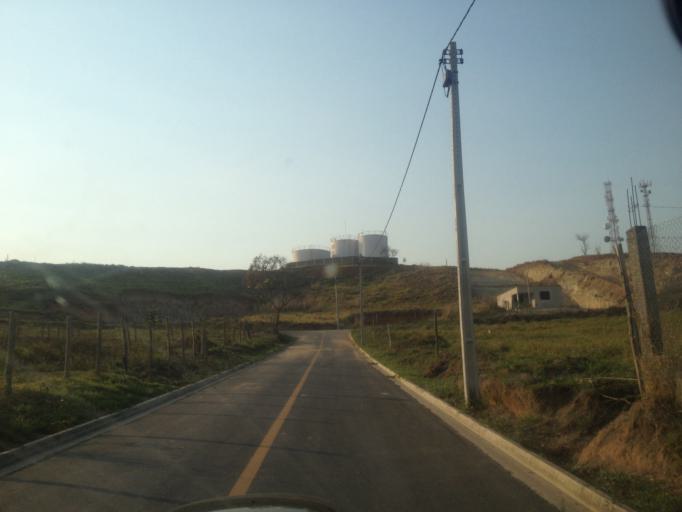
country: BR
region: Rio de Janeiro
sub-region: Porto Real
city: Porto Real
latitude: -22.4350
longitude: -44.3207
